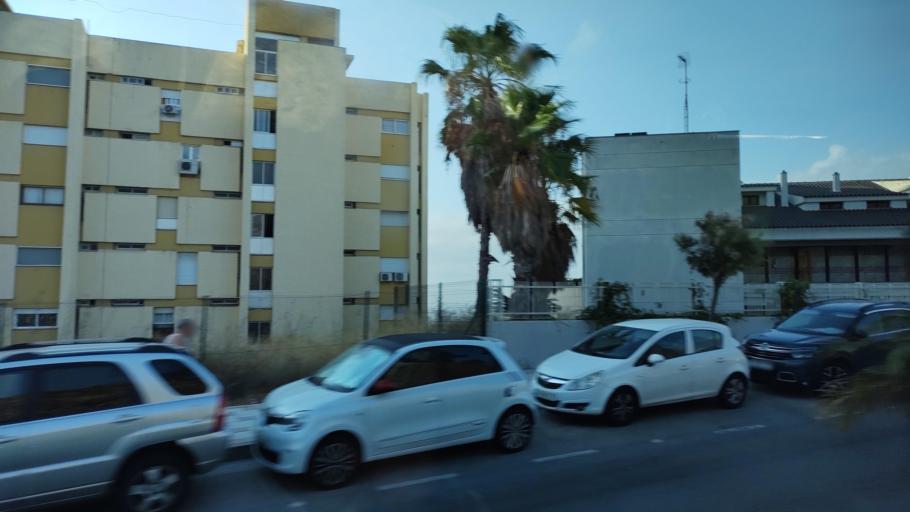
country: ES
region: Andalusia
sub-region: Provincia de Malaga
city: Fuengirola
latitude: 36.5664
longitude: -4.5981
